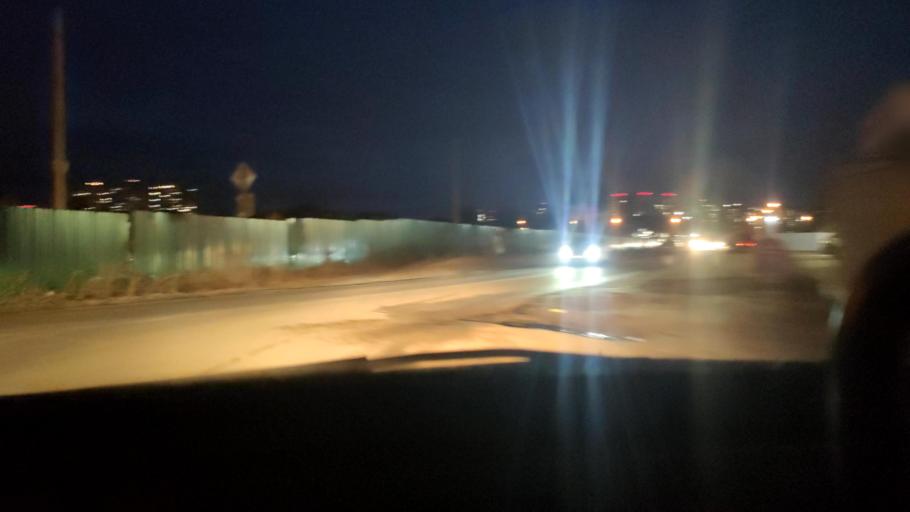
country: RU
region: Voronezj
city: Podgornoye
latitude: 51.7217
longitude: 39.1462
